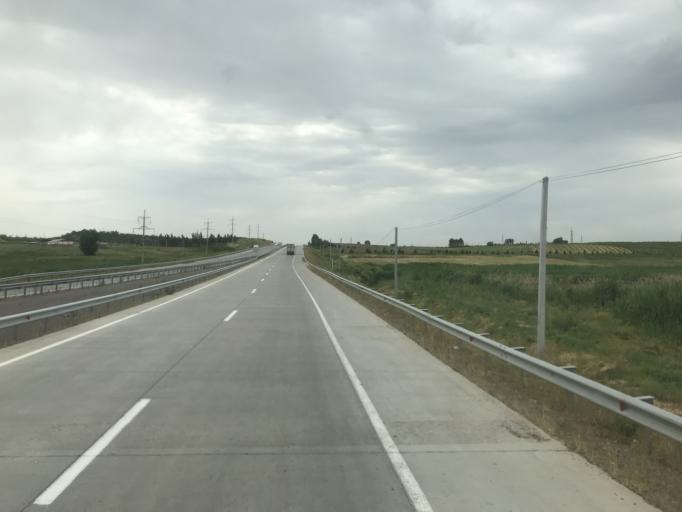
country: UZ
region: Toshkent
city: Qibray
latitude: 41.5226
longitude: 69.3951
